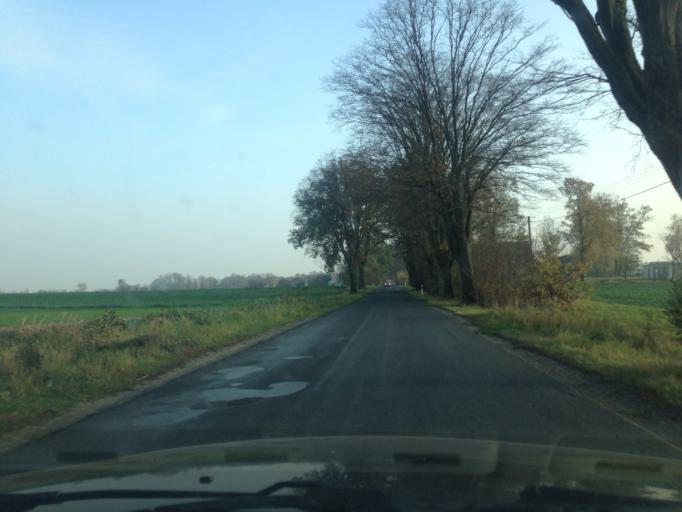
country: PL
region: Kujawsko-Pomorskie
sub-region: Powiat wabrzeski
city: Debowa Laka
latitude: 53.2466
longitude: 19.1291
